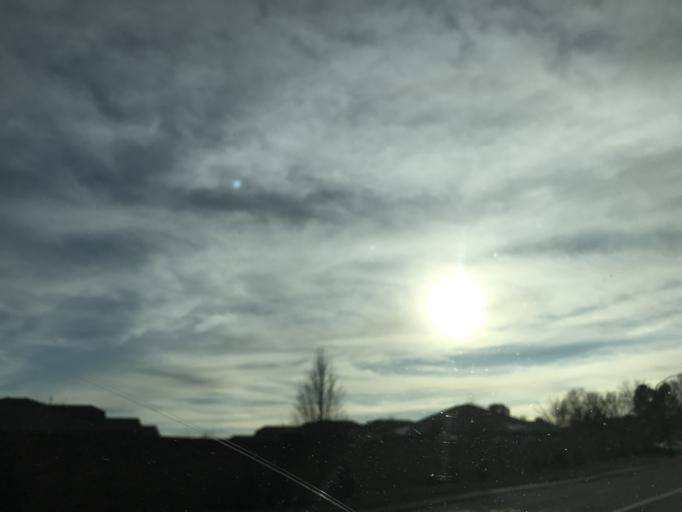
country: US
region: Colorado
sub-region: Arapahoe County
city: Columbine Valley
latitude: 39.6101
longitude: -105.0340
